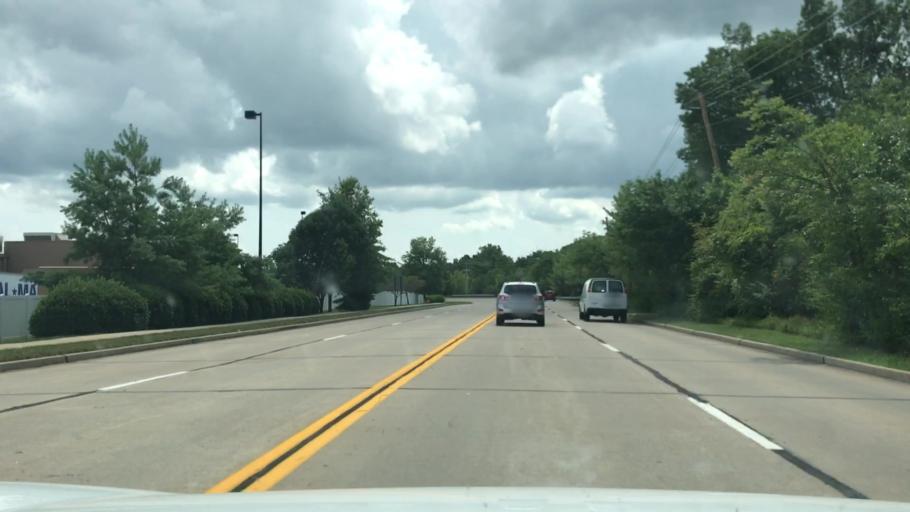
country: US
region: Missouri
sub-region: Saint Charles County
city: O'Fallon
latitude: 38.7945
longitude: -90.7037
